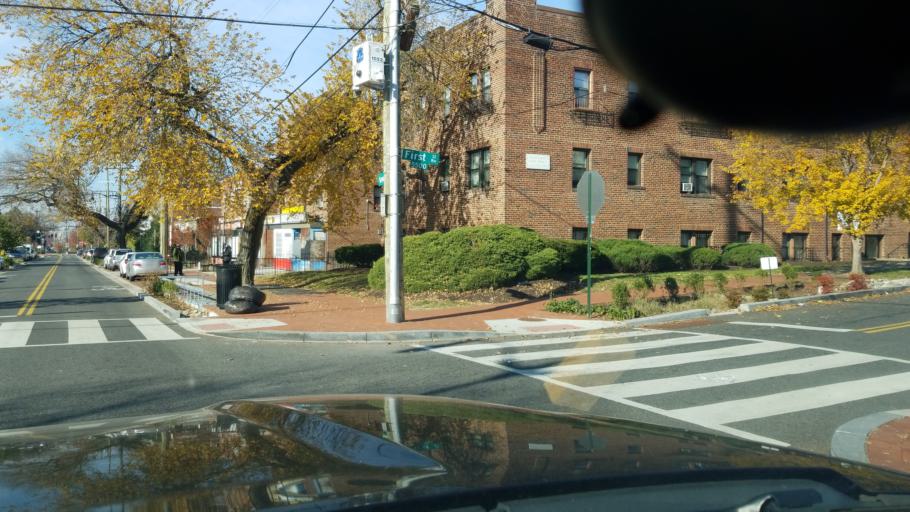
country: US
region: Maryland
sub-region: Montgomery County
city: Takoma Park
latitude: 38.9566
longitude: -77.0116
